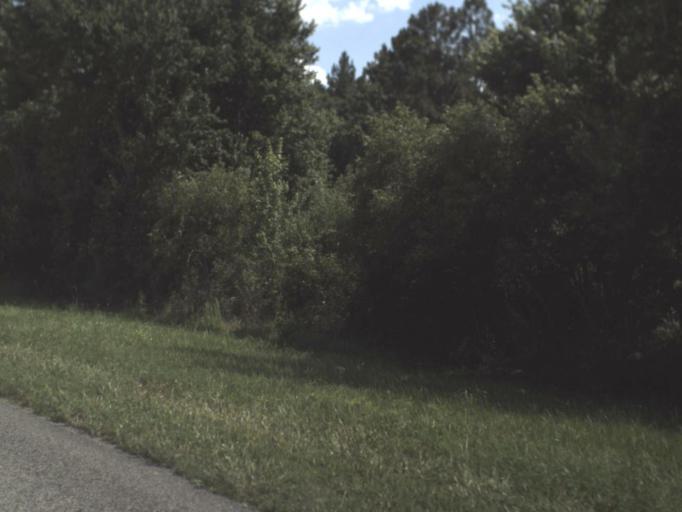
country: US
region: Florida
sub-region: Alachua County
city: Waldo
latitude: 29.7053
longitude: -82.1351
